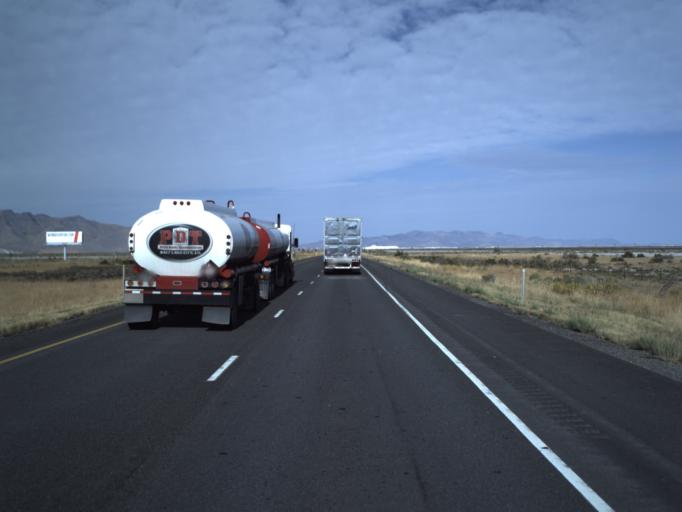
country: US
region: Utah
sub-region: Tooele County
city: Grantsville
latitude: 40.6908
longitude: -112.4613
